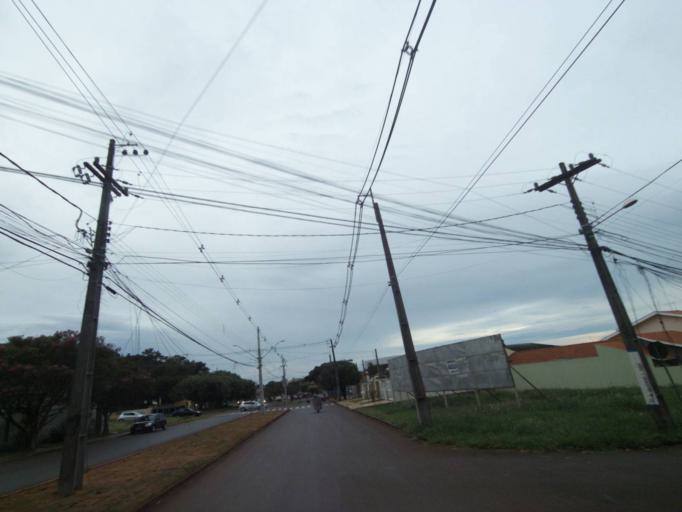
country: BR
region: Parana
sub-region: Campo Mourao
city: Campo Mourao
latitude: -24.0401
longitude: -52.3652
